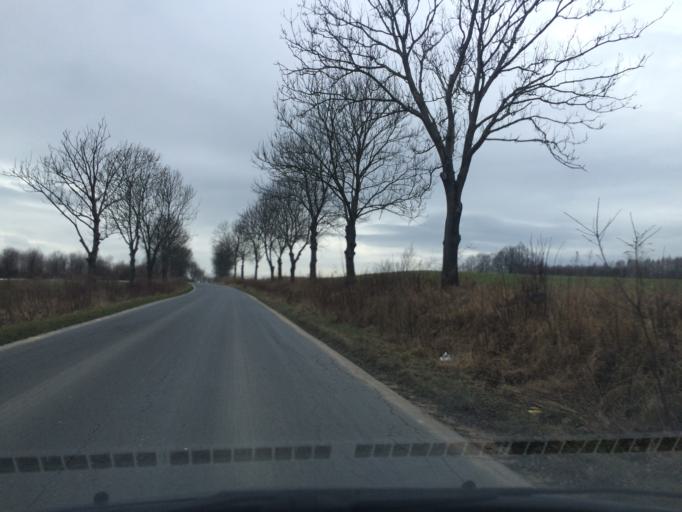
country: PL
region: Lower Silesian Voivodeship
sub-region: Powiat lwowecki
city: Lwowek Slaski
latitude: 51.1215
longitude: 15.5124
